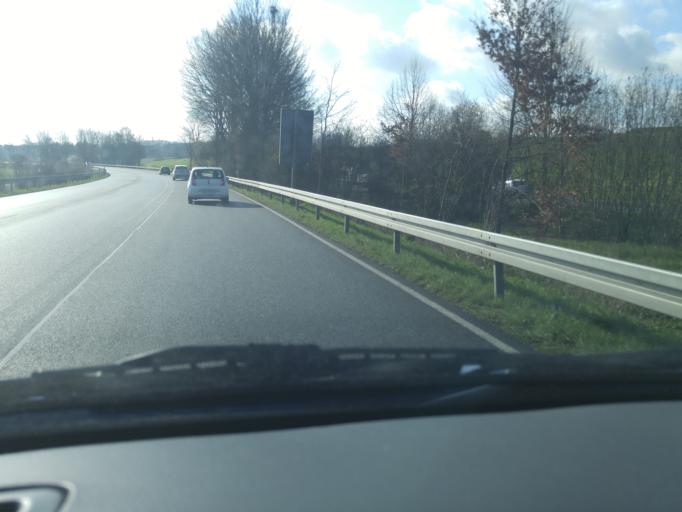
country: DE
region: Hesse
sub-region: Regierungsbezirk Kassel
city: Grossenluder
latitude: 50.5778
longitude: 9.5500
